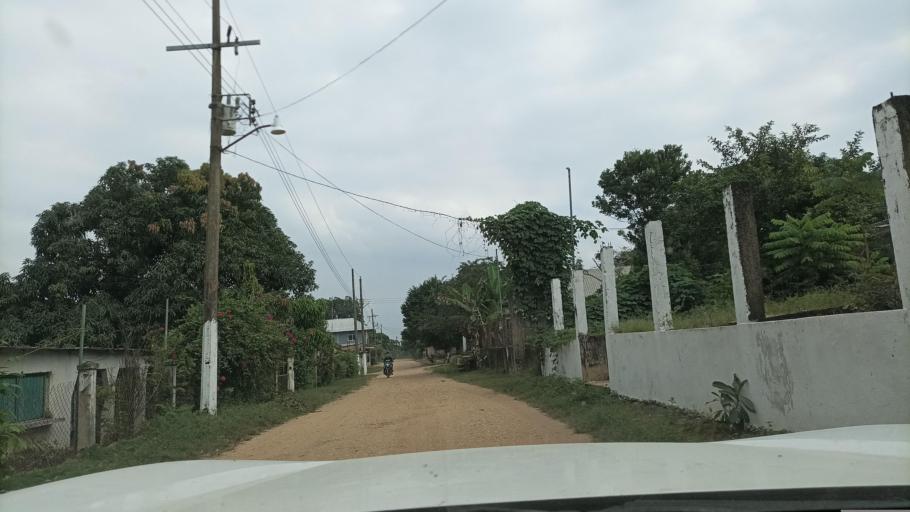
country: MX
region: Veracruz
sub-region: Texistepec
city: San Lorenzo Tenochtitlan
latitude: 17.7734
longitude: -94.8056
